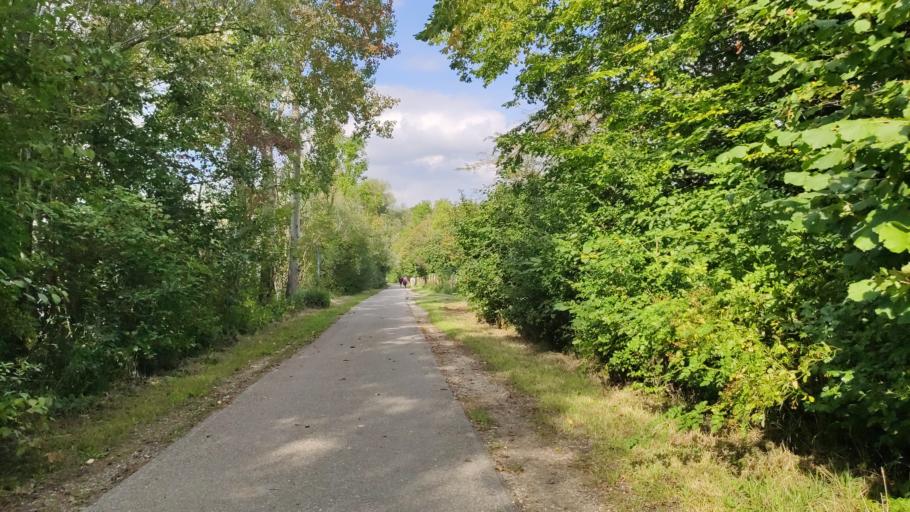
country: DE
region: Bavaria
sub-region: Upper Bavaria
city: Kaufering
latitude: 48.1006
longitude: 10.8682
